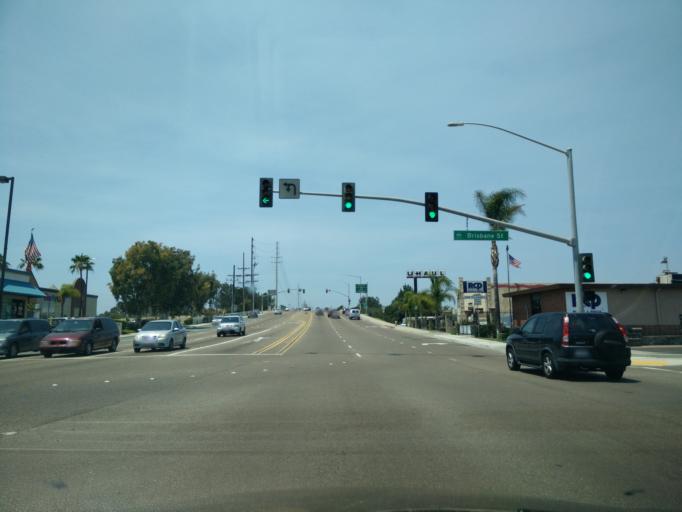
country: US
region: California
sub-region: San Diego County
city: Chula Vista
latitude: 32.6525
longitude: -117.0887
